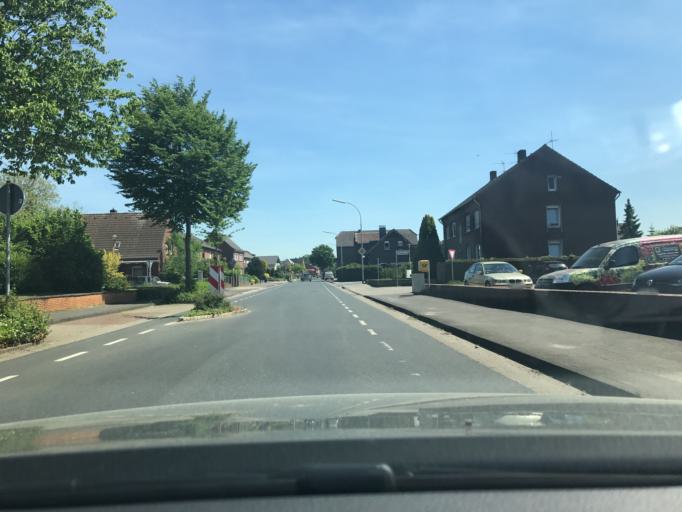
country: DE
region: North Rhine-Westphalia
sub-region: Regierungsbezirk Dusseldorf
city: Wachtendonk
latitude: 51.4088
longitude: 6.3400
